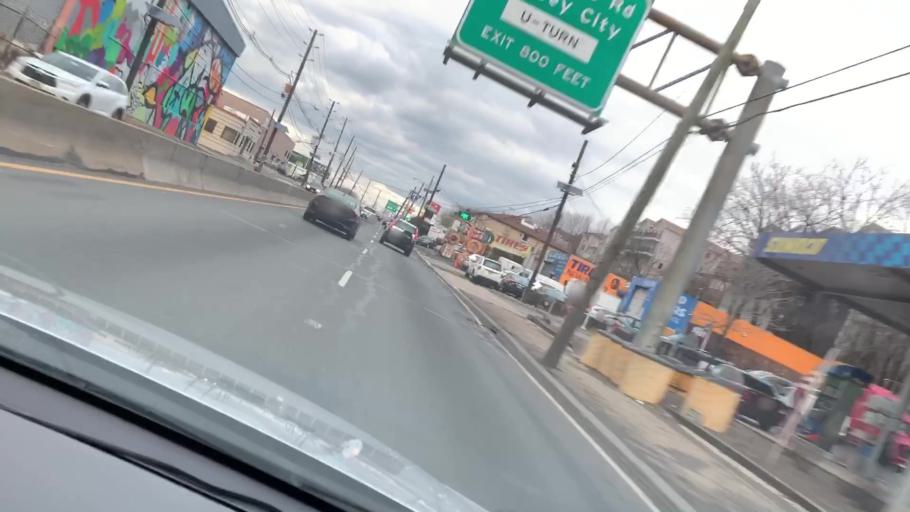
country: US
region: New Jersey
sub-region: Hudson County
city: Hoboken
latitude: 40.7547
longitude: -74.0559
